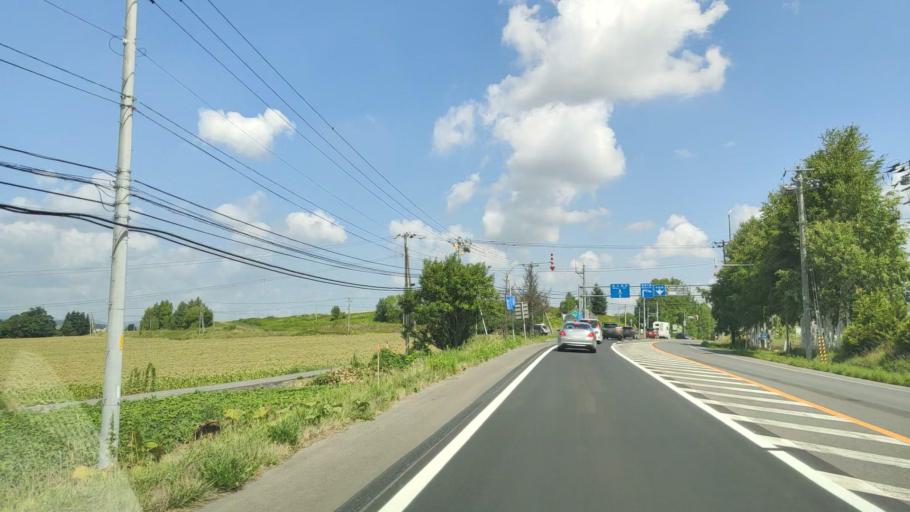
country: JP
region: Hokkaido
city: Shimo-furano
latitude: 43.5442
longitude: 142.4385
